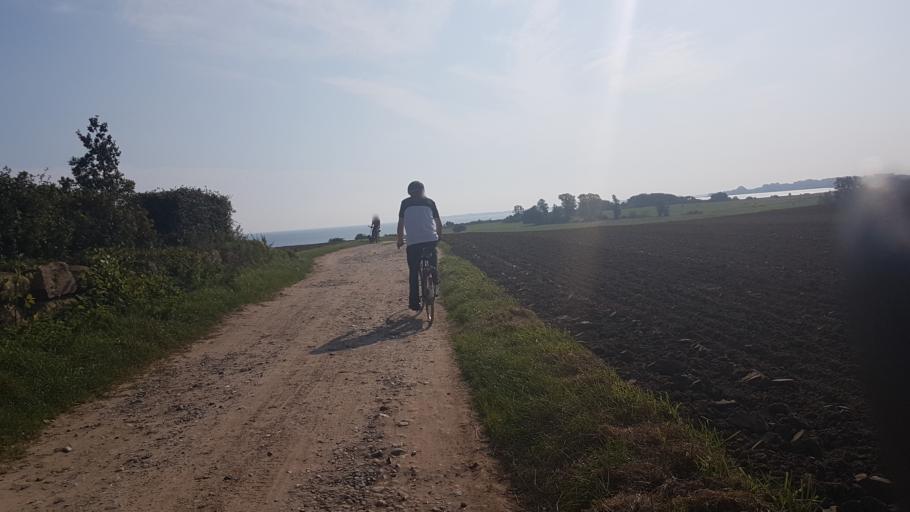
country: DE
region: Mecklenburg-Vorpommern
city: Putbus
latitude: 54.3148
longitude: 13.4374
